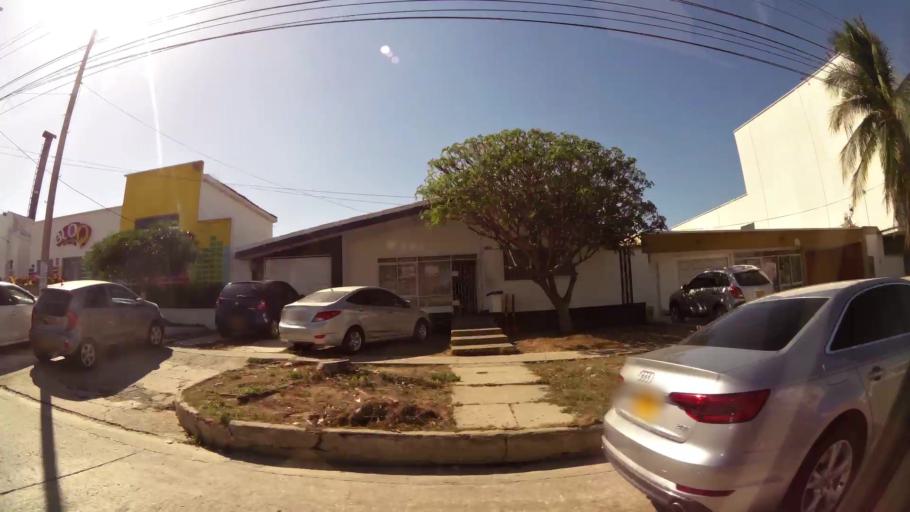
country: CO
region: Atlantico
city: Barranquilla
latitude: 11.0028
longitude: -74.8276
